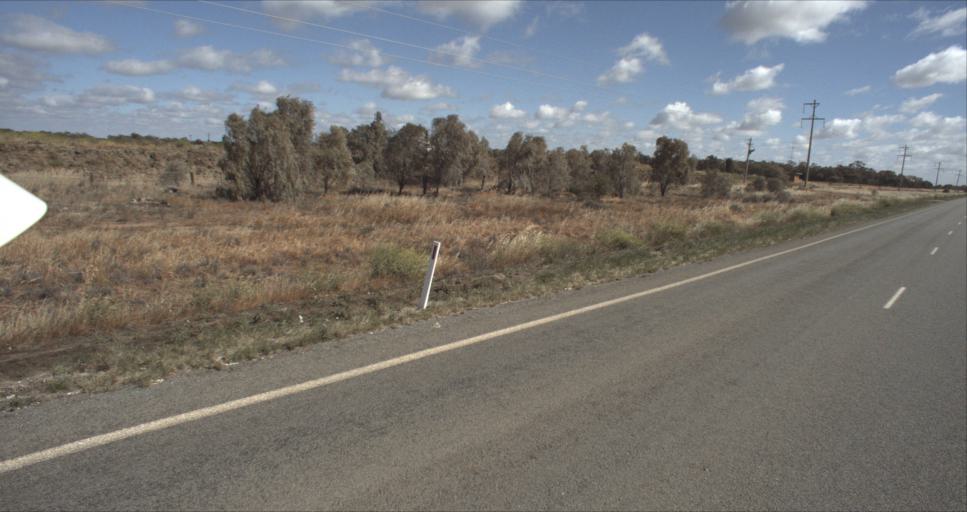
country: AU
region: New South Wales
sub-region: Murrumbidgee Shire
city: Darlington Point
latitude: -34.5500
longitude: 146.1708
